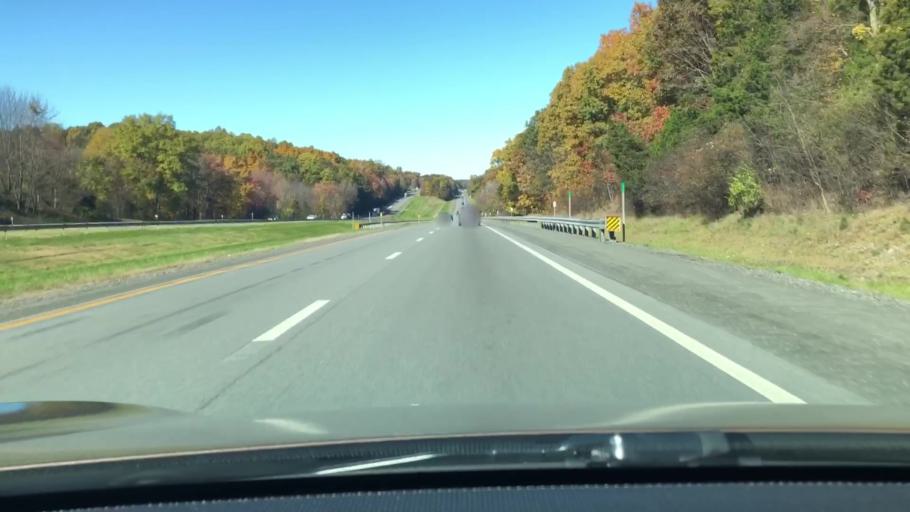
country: US
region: New York
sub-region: Orange County
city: Vails Gate
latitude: 41.4649
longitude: -74.0694
